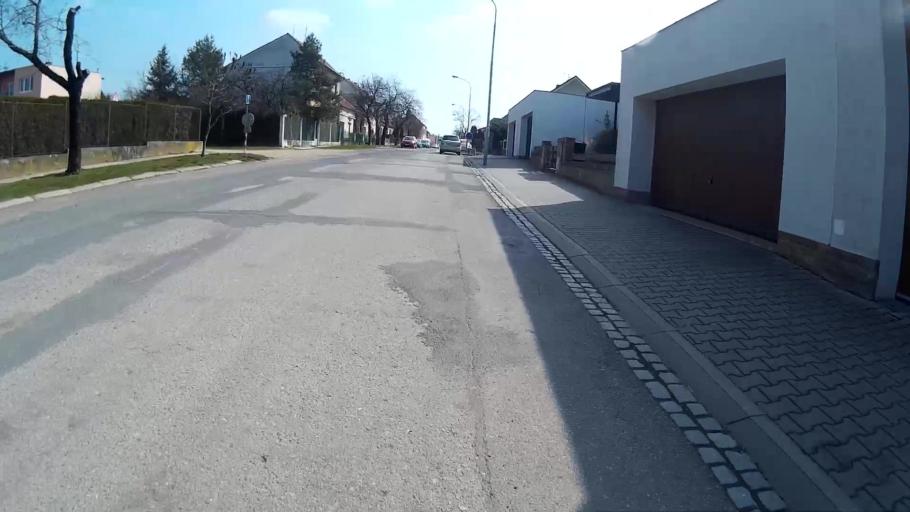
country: CZ
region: South Moravian
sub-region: Mesto Brno
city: Mokra Hora
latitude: 49.2583
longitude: 16.6193
